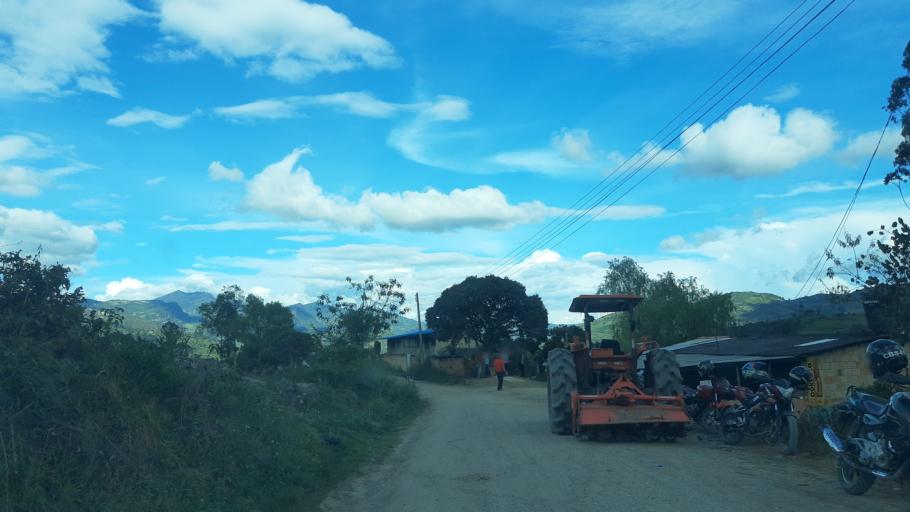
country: CO
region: Cundinamarca
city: Macheta
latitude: 5.0714
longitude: -73.6242
